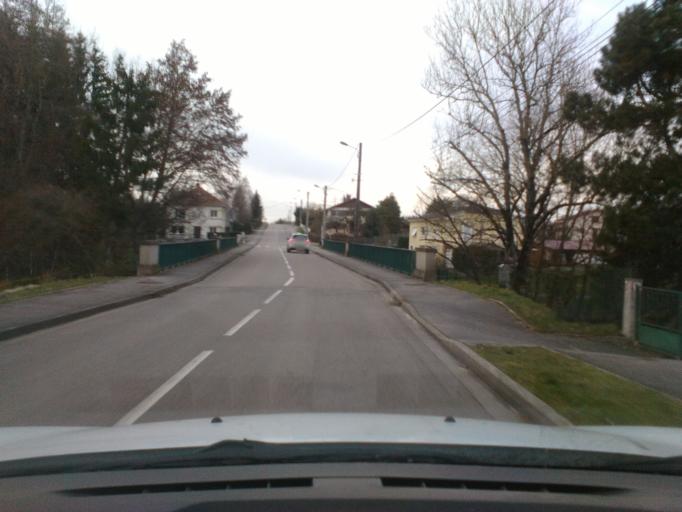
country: FR
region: Lorraine
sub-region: Departement des Vosges
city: Portieux
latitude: 48.3481
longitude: 6.3409
